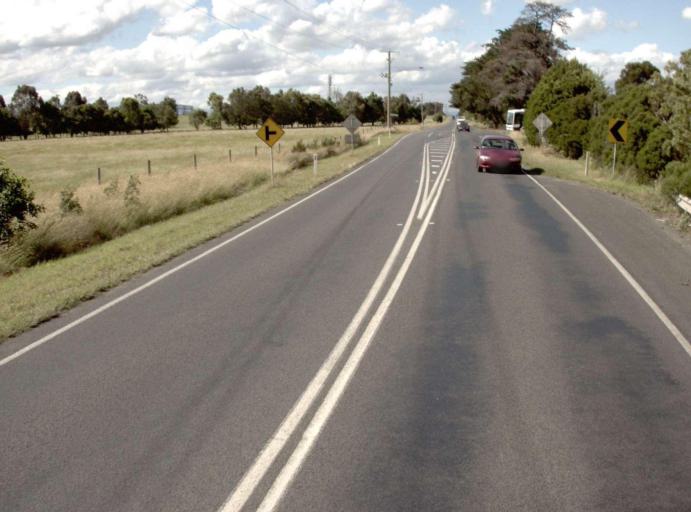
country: AU
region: Victoria
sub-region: Latrobe
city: Morwell
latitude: -38.2922
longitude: 146.4293
